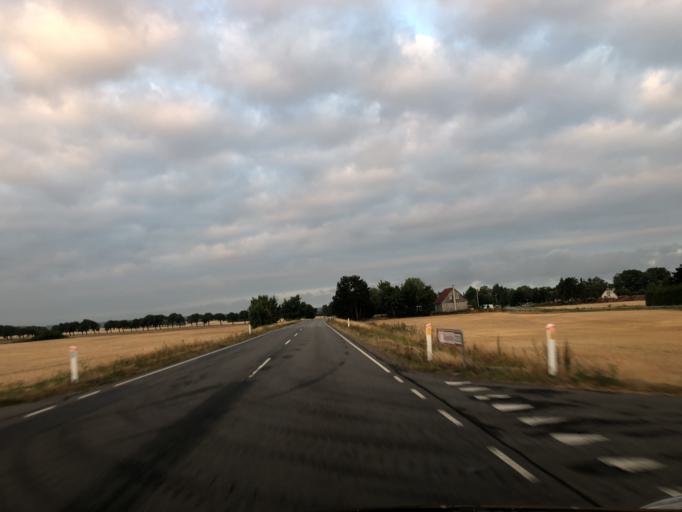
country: DK
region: Zealand
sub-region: Slagelse Kommune
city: Slagelse
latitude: 55.4496
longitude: 11.4312
